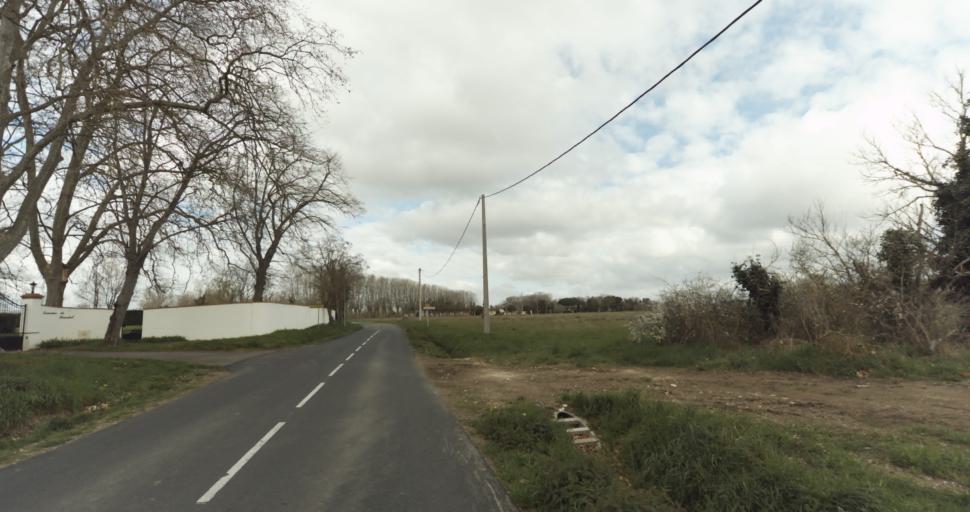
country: FR
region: Midi-Pyrenees
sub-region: Departement de la Haute-Garonne
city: Auterive
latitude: 43.3568
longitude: 1.4589
